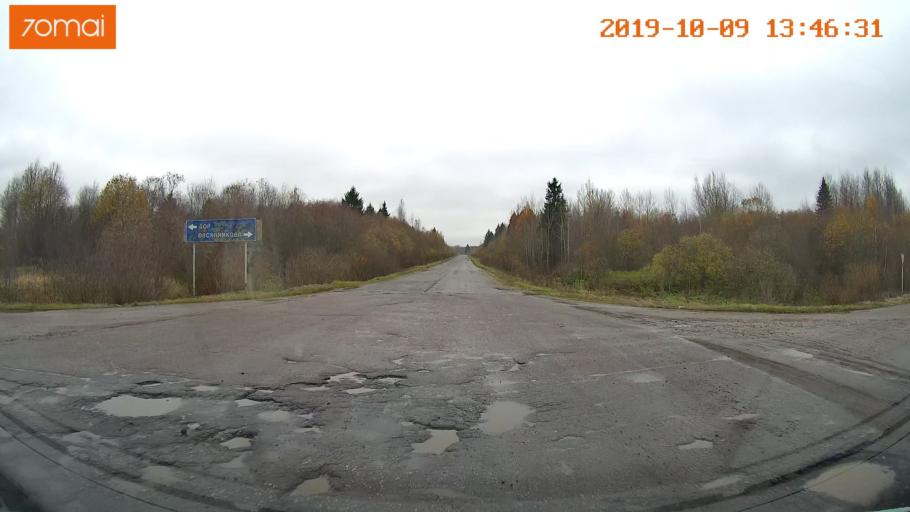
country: RU
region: Kostroma
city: Buy
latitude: 58.3844
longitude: 41.2186
